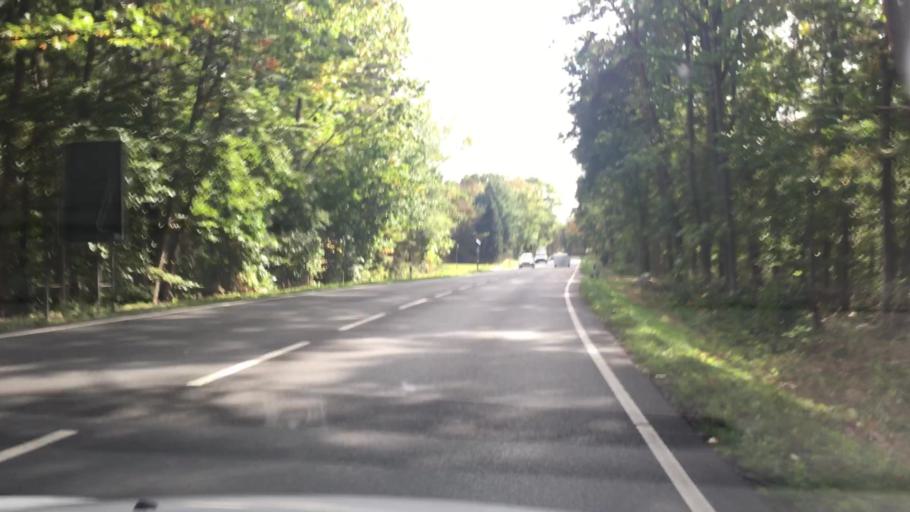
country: DE
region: Lower Saxony
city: Diepholz
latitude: 52.6532
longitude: 8.3366
